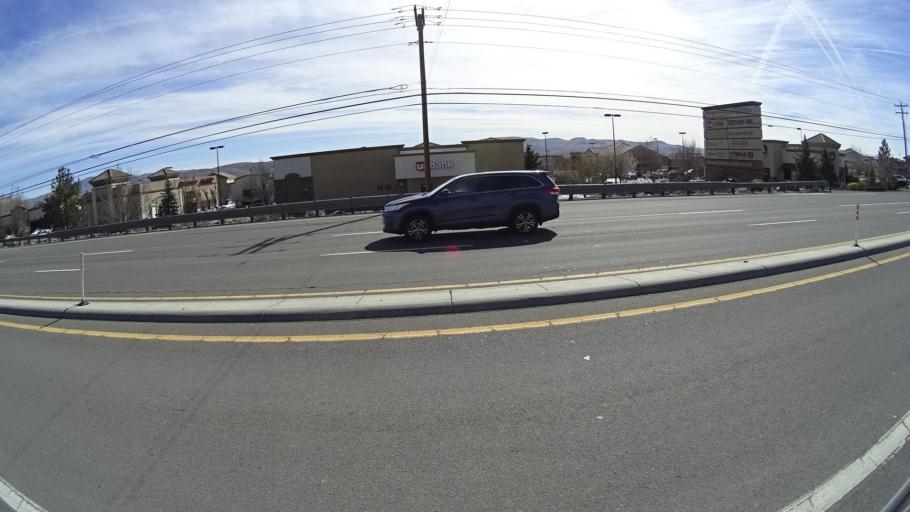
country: US
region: Nevada
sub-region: Washoe County
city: Sun Valley
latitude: 39.5843
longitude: -119.7428
